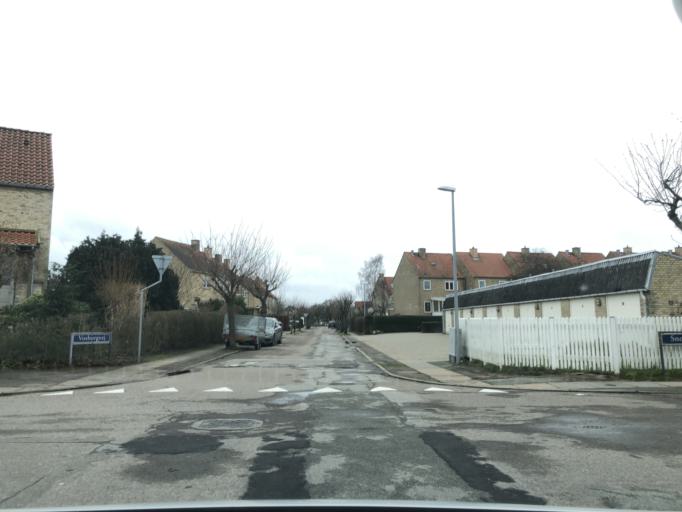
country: DK
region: Capital Region
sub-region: Tarnby Kommune
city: Tarnby
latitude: 55.6206
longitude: 12.6132
